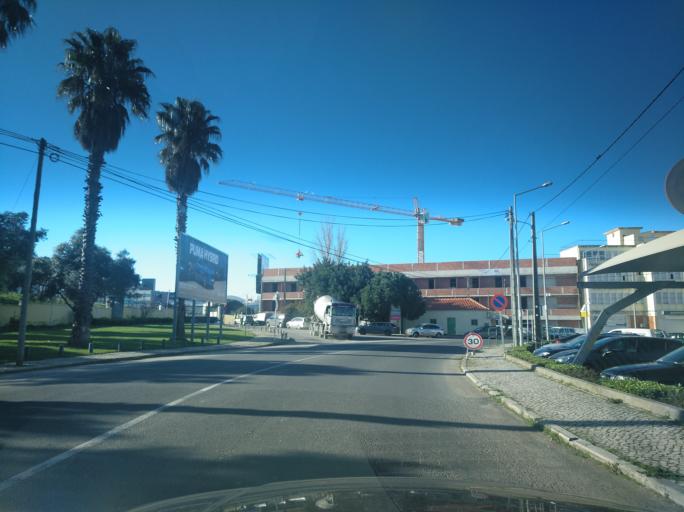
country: PT
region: Lisbon
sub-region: Loures
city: Sacavem
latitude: 38.7853
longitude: -9.1171
